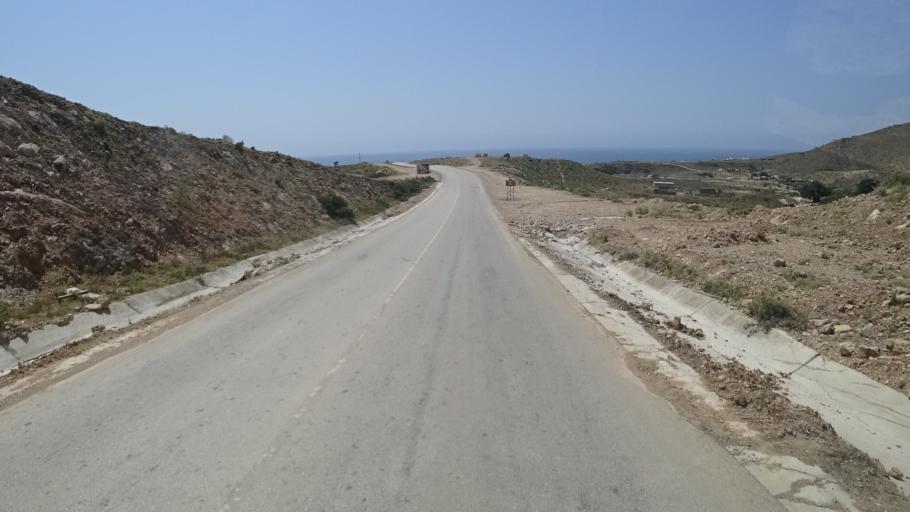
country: OM
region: Zufar
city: Salalah
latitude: 17.0434
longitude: 54.6128
